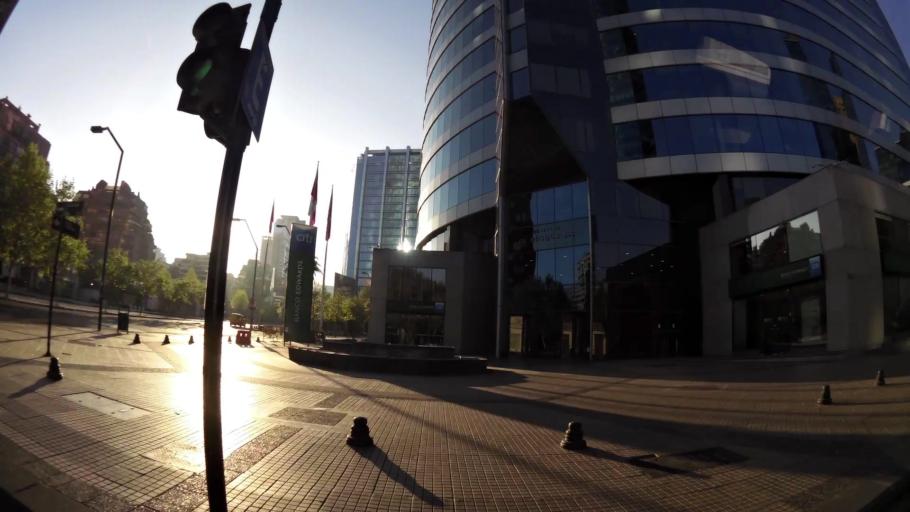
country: CL
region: Santiago Metropolitan
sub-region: Provincia de Santiago
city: Villa Presidente Frei, Nunoa, Santiago, Chile
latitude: -33.4141
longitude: -70.6033
